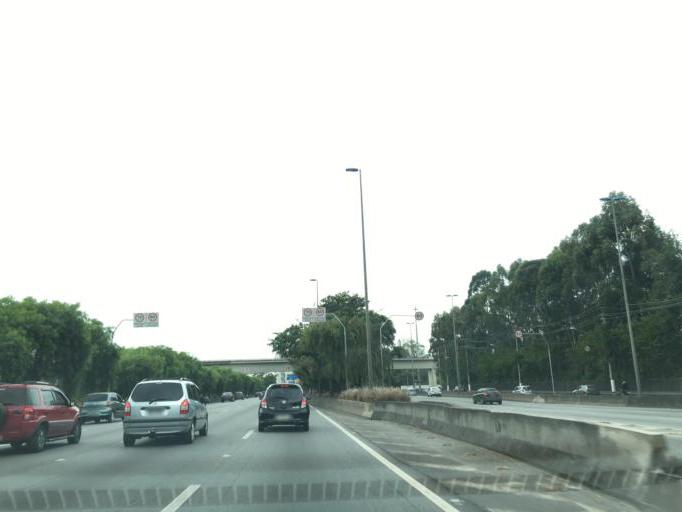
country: BR
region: Sao Paulo
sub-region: Osasco
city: Osasco
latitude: -23.5182
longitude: -46.7381
